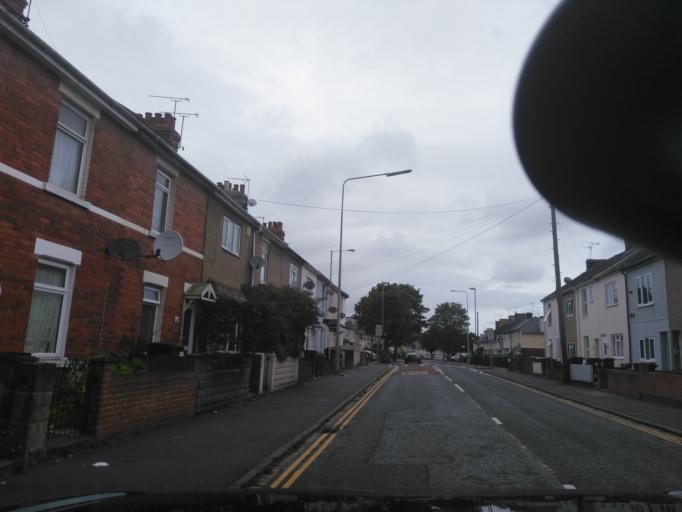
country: GB
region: England
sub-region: Borough of Swindon
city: Swindon
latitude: 51.5726
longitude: -1.7861
